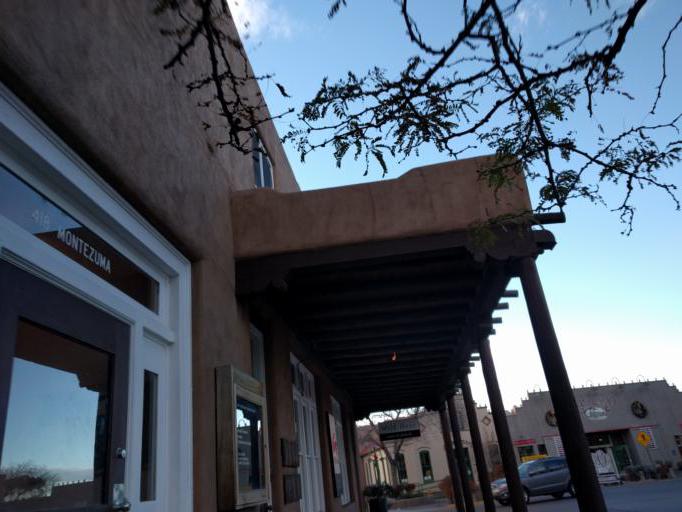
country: US
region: New Mexico
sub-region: Santa Fe County
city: Santa Fe
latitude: 35.6850
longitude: -105.9465
